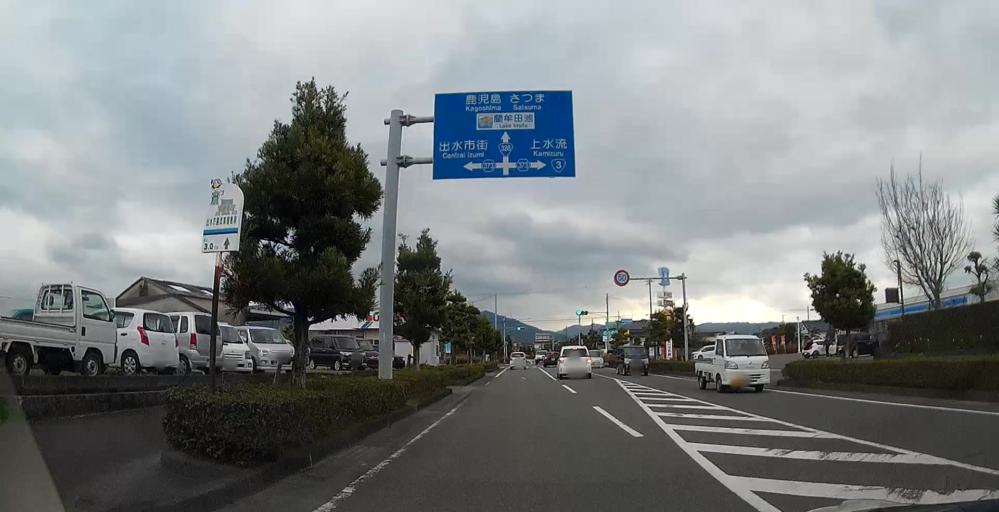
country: JP
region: Kagoshima
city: Izumi
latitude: 32.0830
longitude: 130.3444
